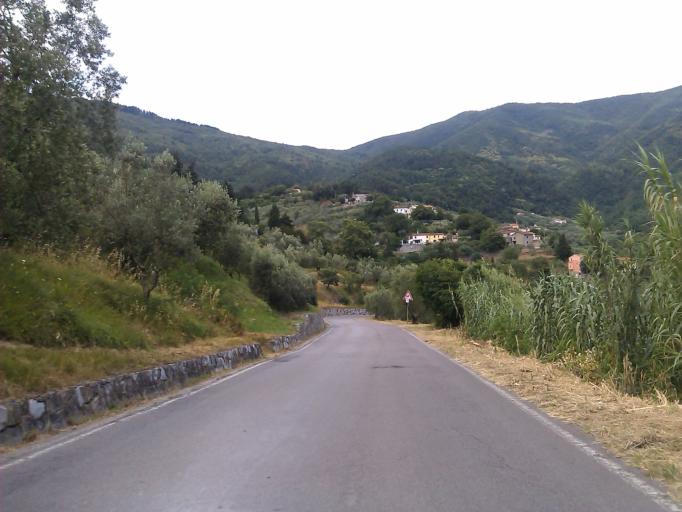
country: IT
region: Tuscany
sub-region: Provincia di Prato
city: Montemurlo
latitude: 43.9611
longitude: 11.0450
